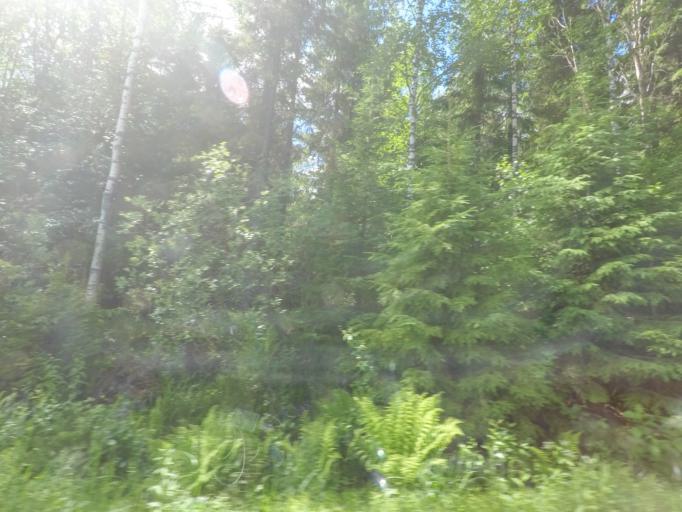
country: FI
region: Central Finland
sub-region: Jyvaeskylae
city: Hankasalmi
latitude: 62.4169
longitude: 26.6404
